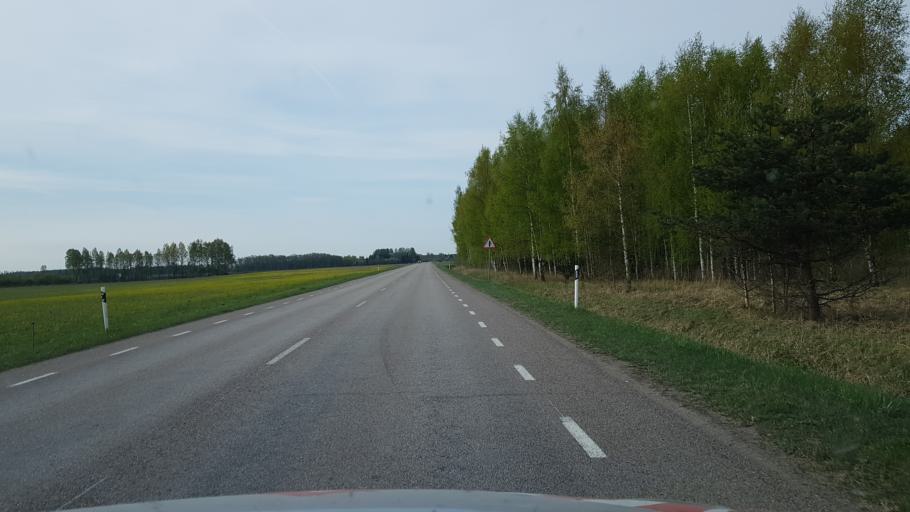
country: EE
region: Paernumaa
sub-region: Audru vald
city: Audru
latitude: 58.3830
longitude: 24.2722
